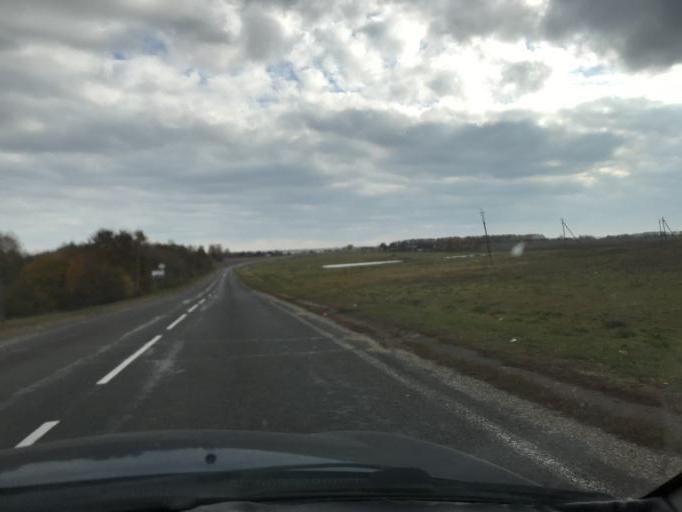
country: BY
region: Grodnenskaya
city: Lida
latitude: 53.7908
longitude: 25.1491
